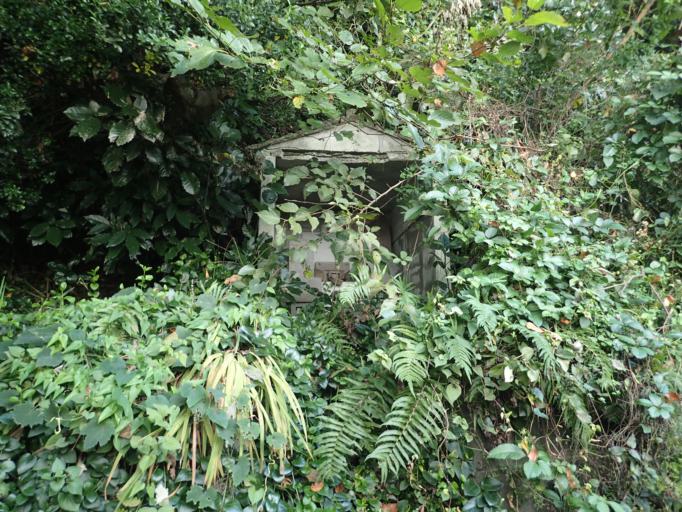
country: JP
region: Kanagawa
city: Hayama
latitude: 35.2845
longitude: 139.5920
